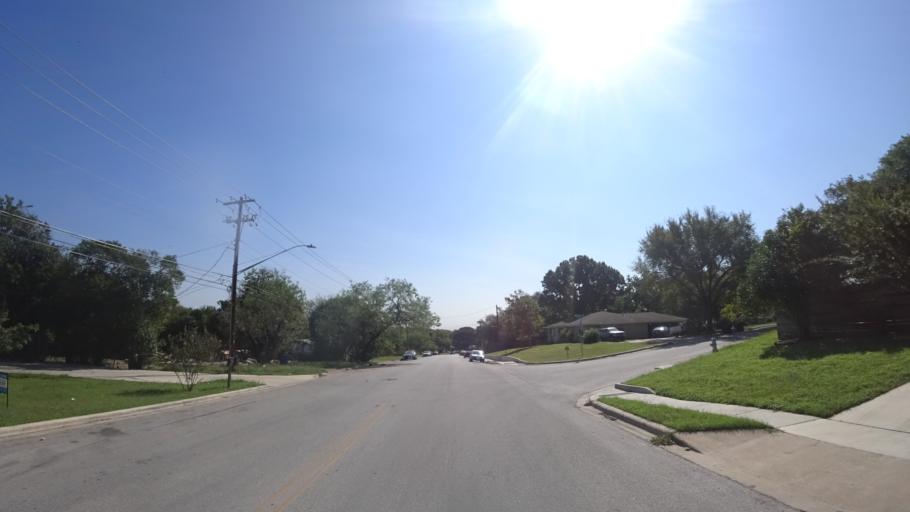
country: US
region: Texas
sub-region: Travis County
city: Austin
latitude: 30.3101
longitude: -97.6728
